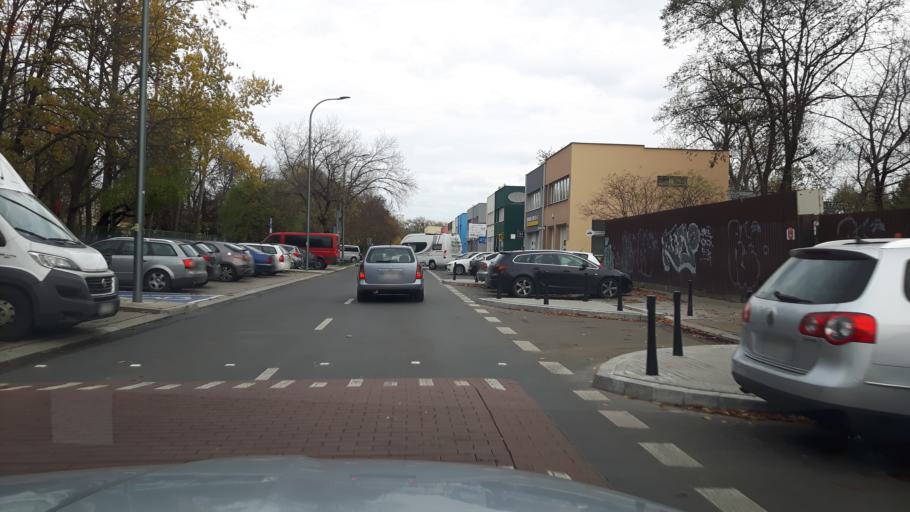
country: PL
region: Masovian Voivodeship
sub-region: Warszawa
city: Mokotow
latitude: 52.1683
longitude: 21.0032
